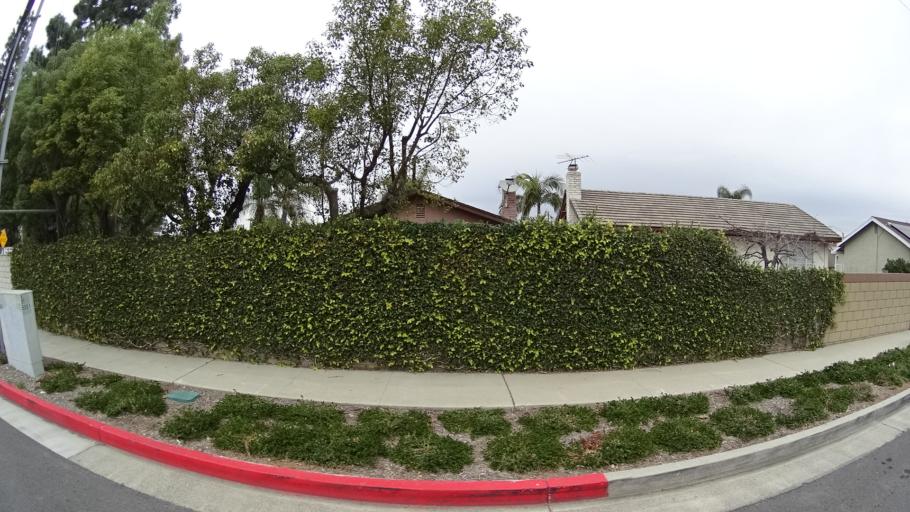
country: US
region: California
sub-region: Orange County
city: Yorba Linda
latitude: 33.8526
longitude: -117.7931
